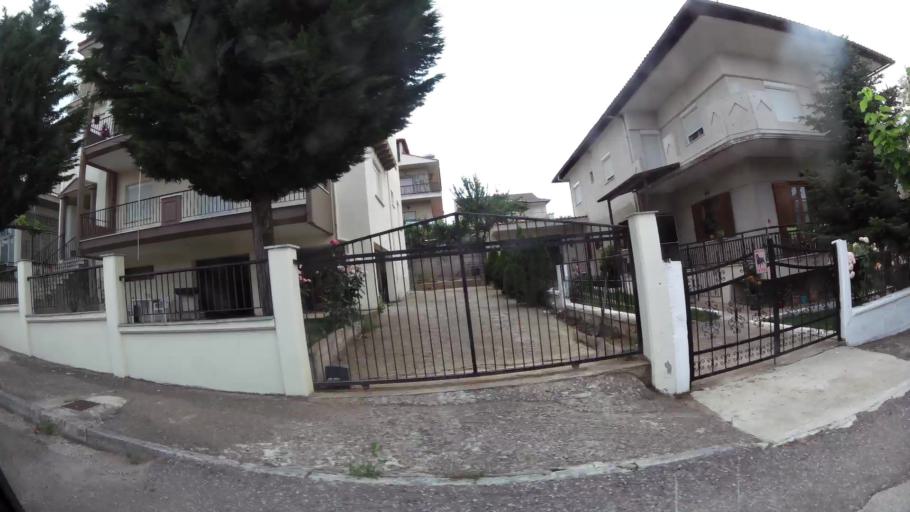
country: GR
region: West Macedonia
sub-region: Nomos Kozanis
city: Koila
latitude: 40.3267
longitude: 21.8230
